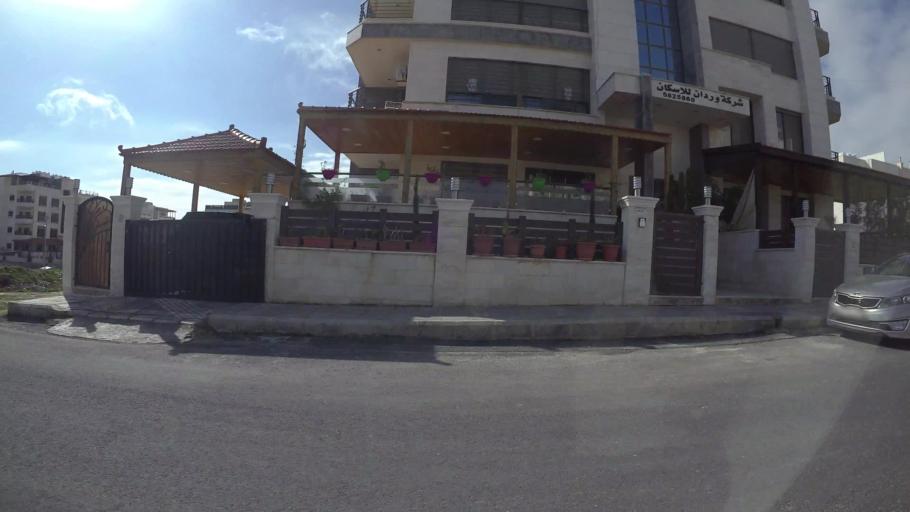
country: JO
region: Amman
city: Al Jubayhah
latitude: 32.0035
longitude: 35.8459
